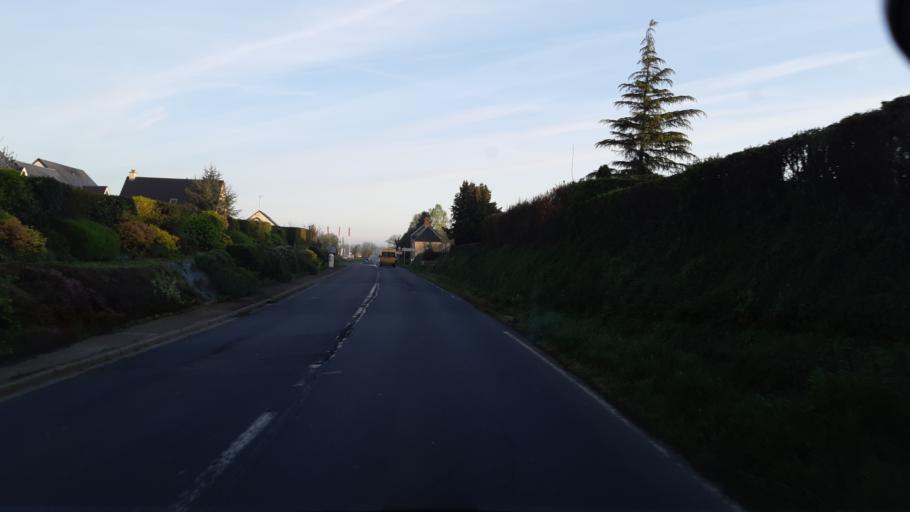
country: FR
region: Lower Normandy
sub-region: Departement de la Manche
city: Agneaux
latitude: 49.0510
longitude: -1.1290
